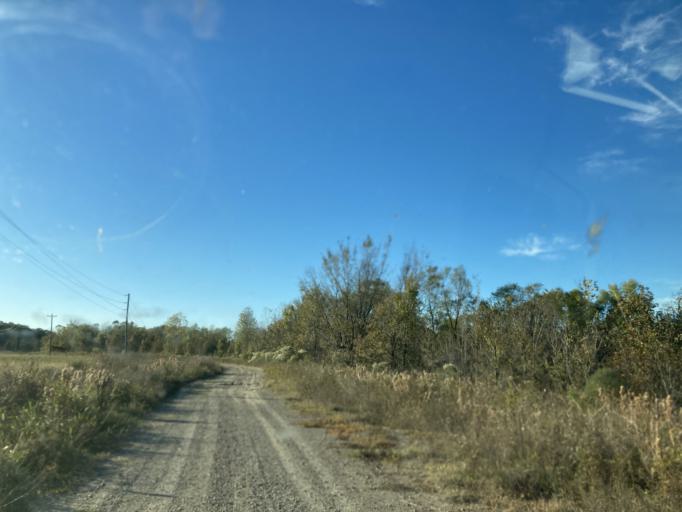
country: US
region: Mississippi
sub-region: Yazoo County
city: Yazoo City
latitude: 32.8921
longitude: -90.4270
